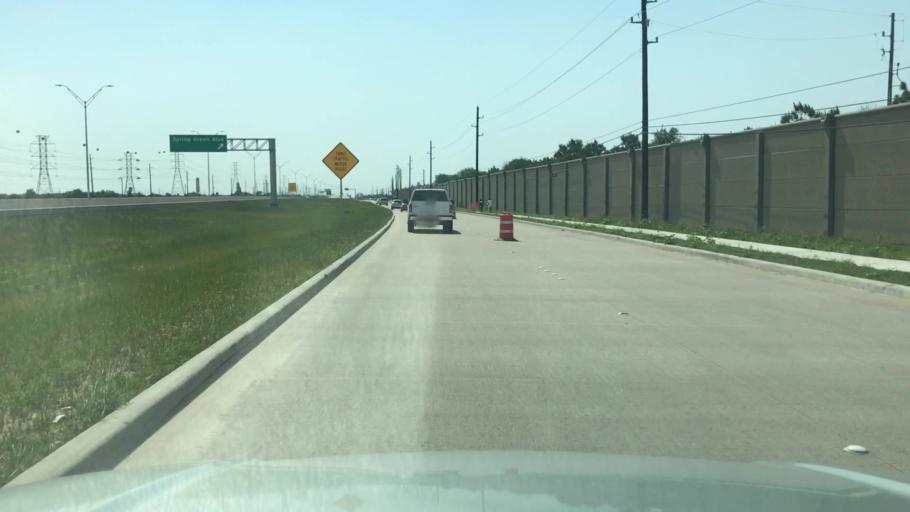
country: US
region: Texas
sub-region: Fort Bend County
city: Cinco Ranch
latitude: 29.6987
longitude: -95.8001
